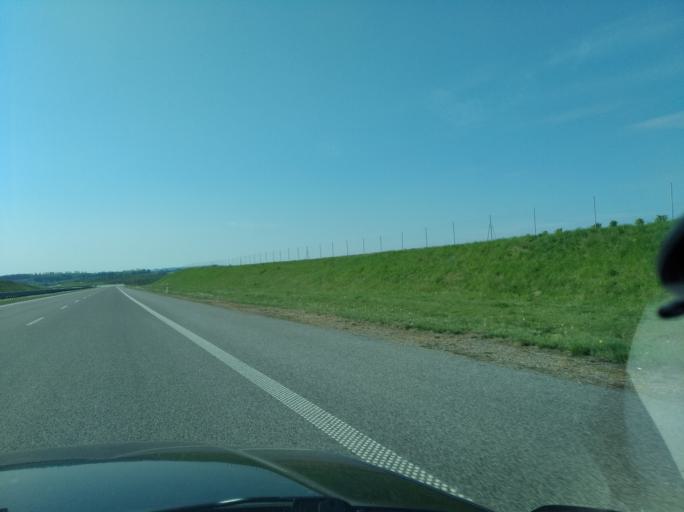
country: PL
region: Subcarpathian Voivodeship
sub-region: Powiat jaroslawski
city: Pawlosiow
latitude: 49.9572
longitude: 22.6604
